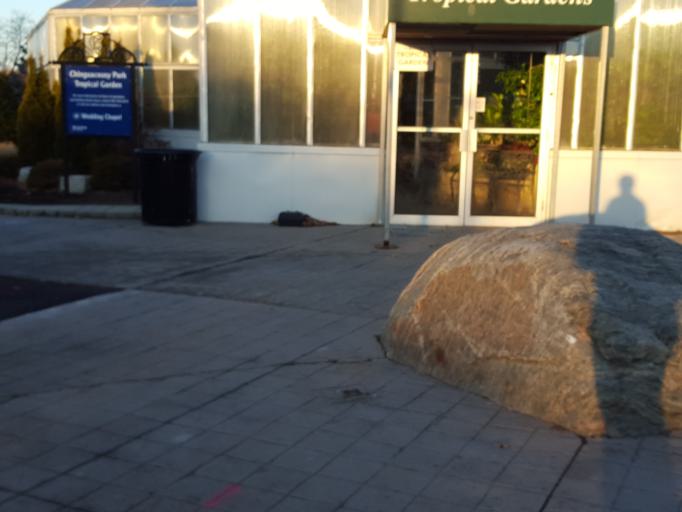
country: CA
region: Ontario
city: Brampton
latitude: 43.7228
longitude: -79.7211
